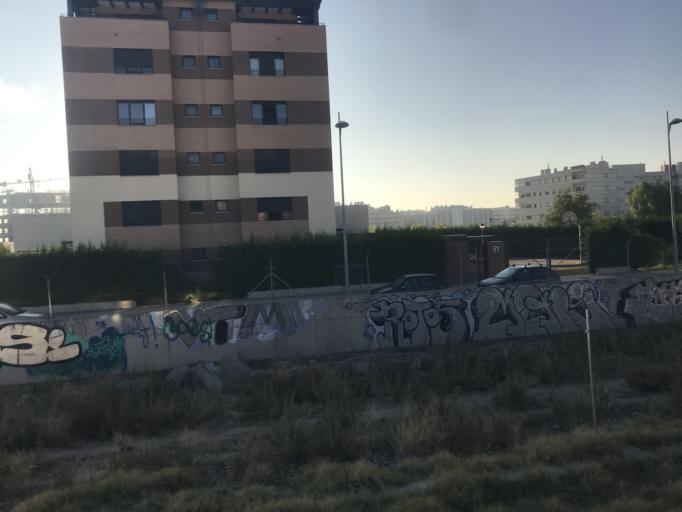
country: ES
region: Castille and Leon
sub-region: Provincia de Valladolid
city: Valladolid
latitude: 41.6563
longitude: -4.7068
